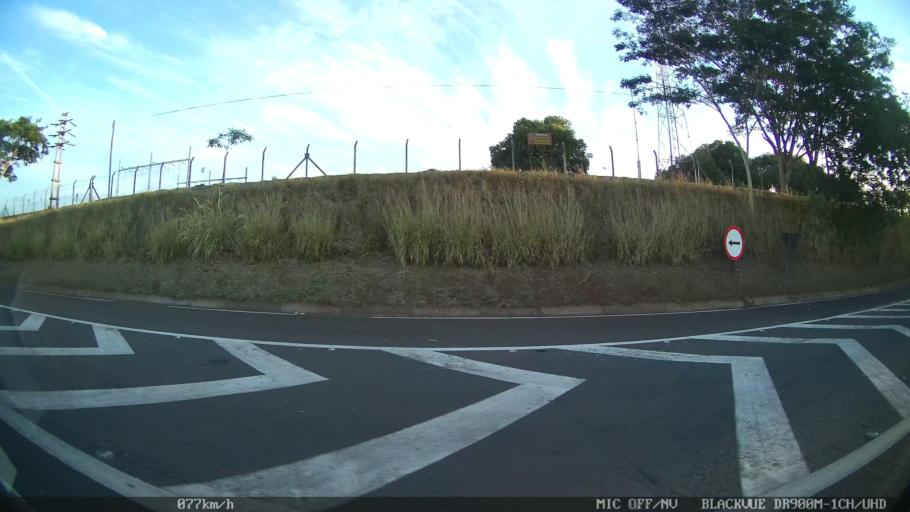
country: BR
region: Sao Paulo
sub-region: Catanduva
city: Catanduva
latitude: -21.1357
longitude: -49.0183
